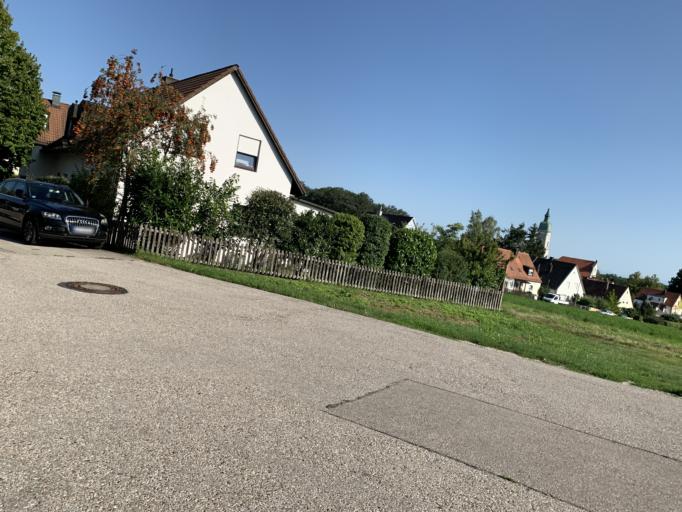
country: DE
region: Bavaria
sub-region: Upper Bavaria
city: Freising
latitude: 48.4100
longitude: 11.7567
